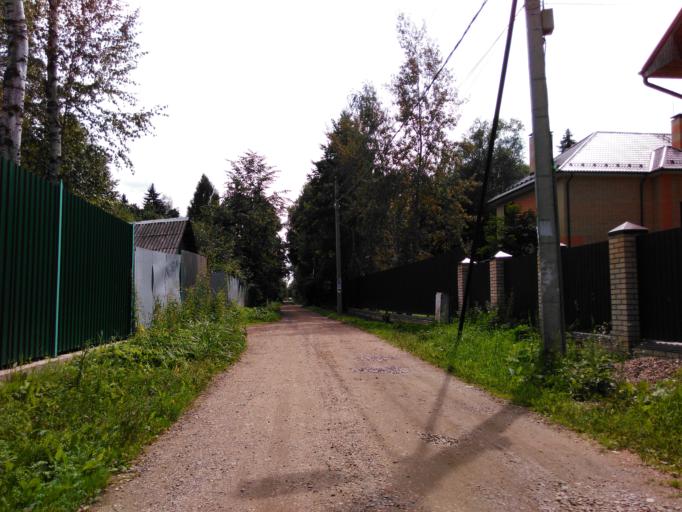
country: RU
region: Moskovskaya
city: Pravdinskiy
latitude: 56.0587
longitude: 37.8391
